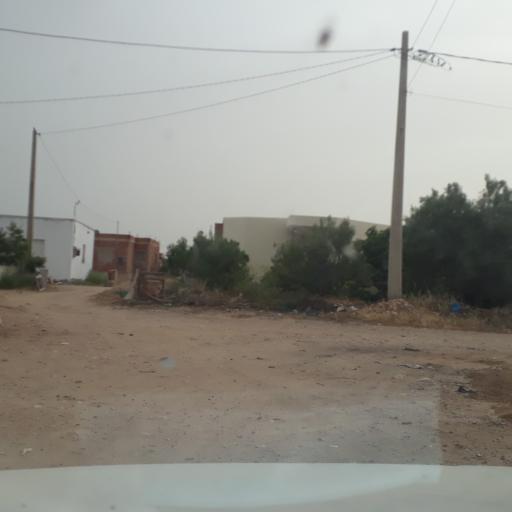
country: TN
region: Safaqis
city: Al Qarmadah
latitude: 34.8285
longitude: 10.7758
